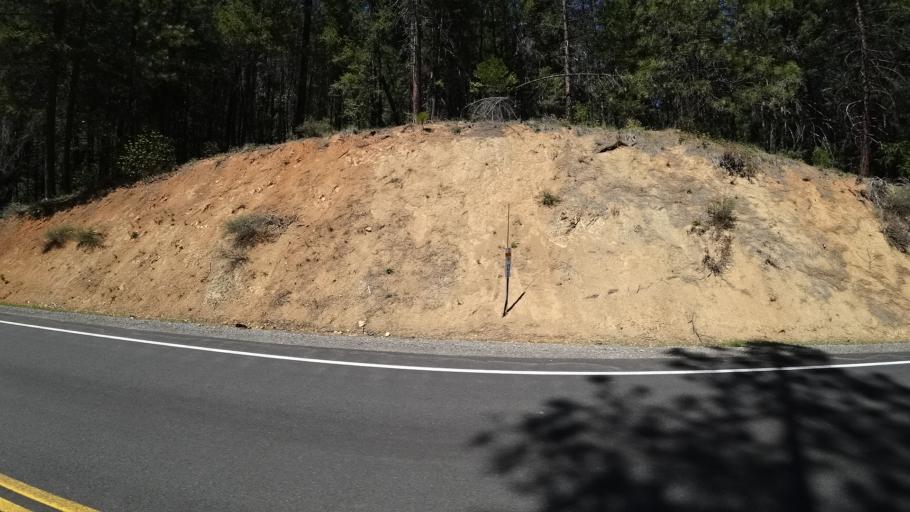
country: US
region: California
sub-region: Trinity County
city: Lewiston
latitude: 40.9061
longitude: -122.7855
